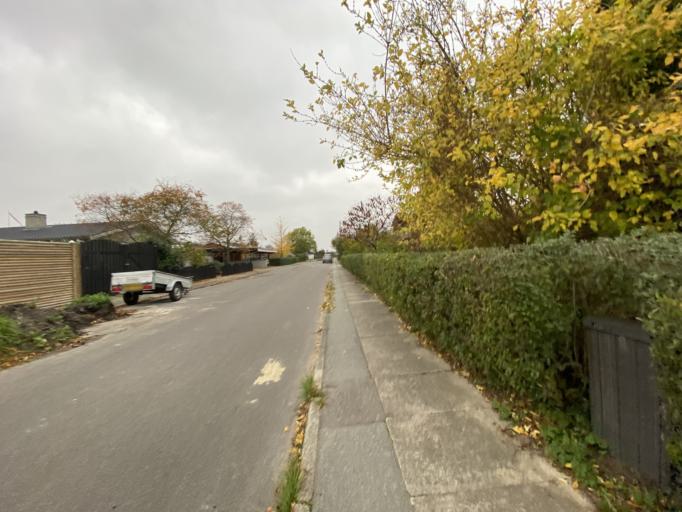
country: DK
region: Capital Region
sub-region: Dragor Kommune
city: Dragor
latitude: 55.5894
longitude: 12.6433
